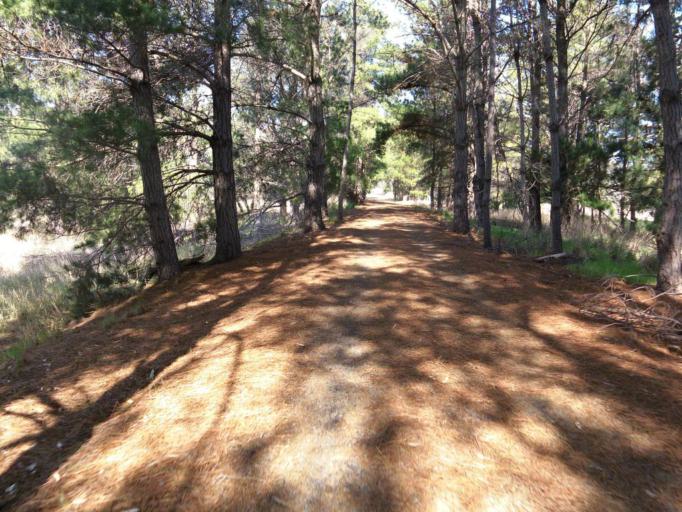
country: AU
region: Victoria
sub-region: Murrindindi
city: Alexandra
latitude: -36.9989
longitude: 145.7440
